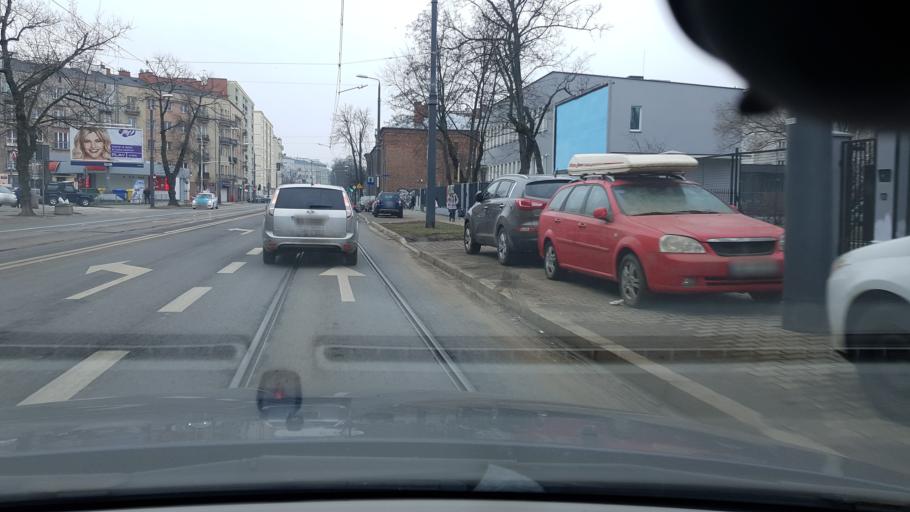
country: PL
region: Masovian Voivodeship
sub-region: Warszawa
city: Praga Polnoc
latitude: 52.2633
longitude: 21.0381
